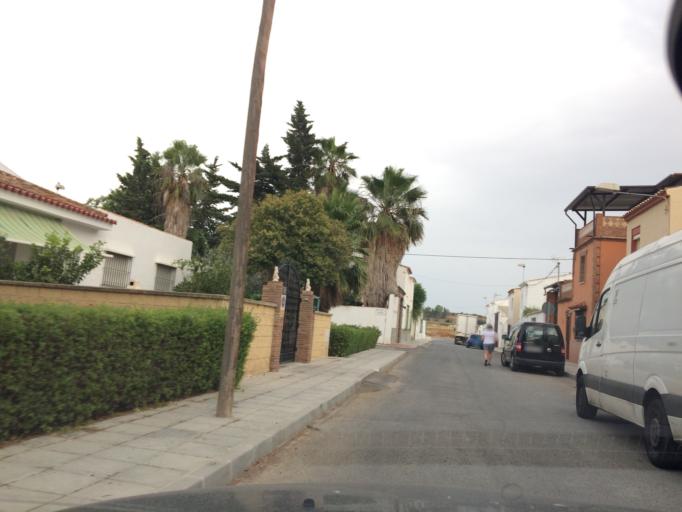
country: ES
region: Andalusia
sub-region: Provincia de Malaga
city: Estacion de Cartama
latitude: 36.7300
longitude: -4.5716
